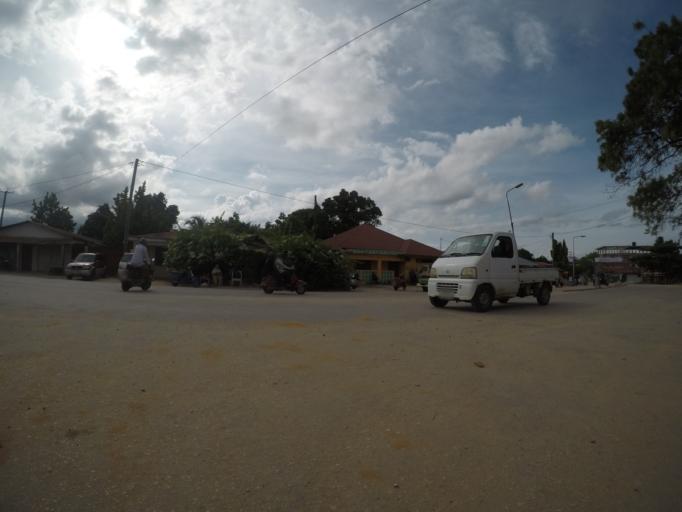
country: TZ
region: Pemba South
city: Chake Chake
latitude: -5.2356
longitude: 39.7778
